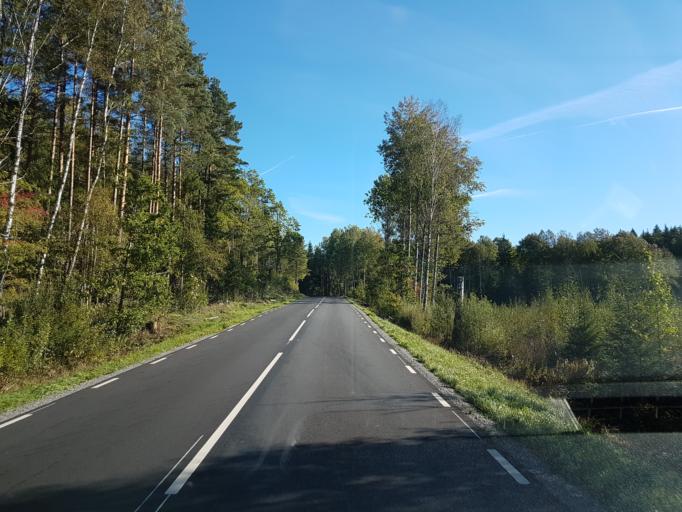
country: SE
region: OEstergoetland
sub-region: Atvidabergs Kommun
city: Atvidaberg
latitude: 58.1797
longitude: 16.0729
